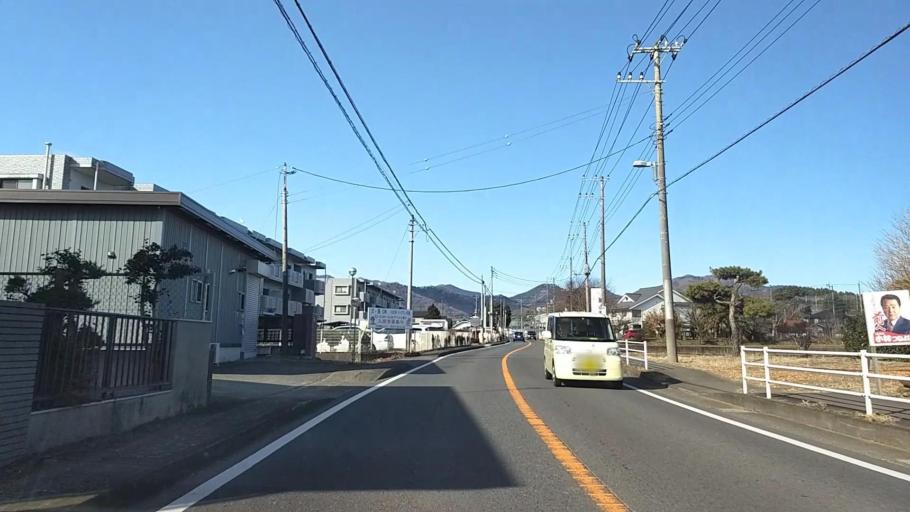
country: JP
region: Kanagawa
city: Atsugi
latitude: 35.4690
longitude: 139.3284
